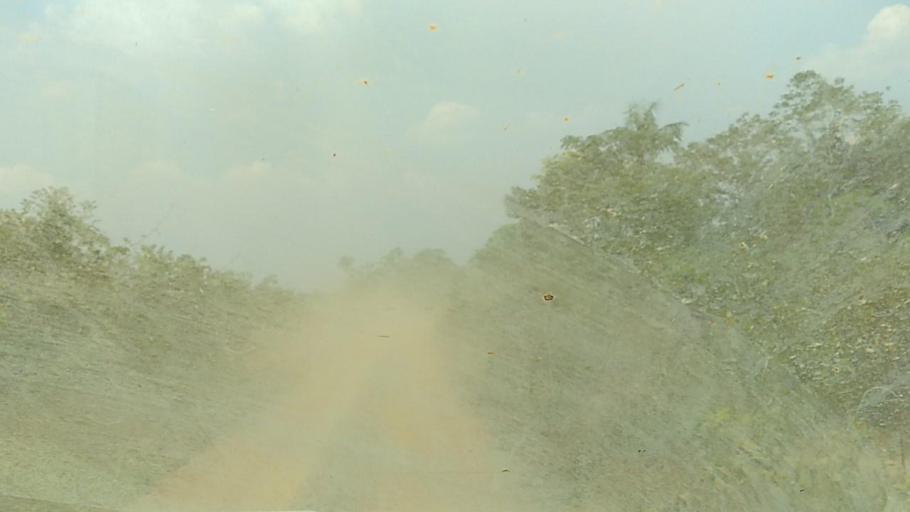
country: BR
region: Rondonia
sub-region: Porto Velho
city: Porto Velho
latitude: -8.7732
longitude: -63.1936
